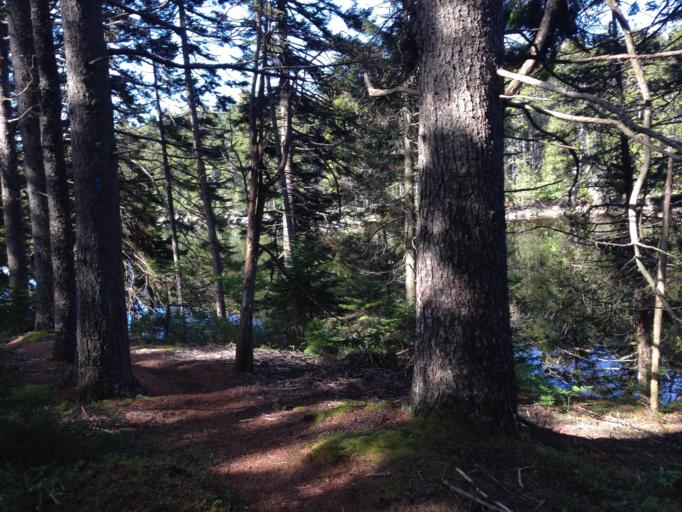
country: US
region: Maine
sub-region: Hancock County
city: Gouldsboro
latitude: 44.3890
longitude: -68.0744
